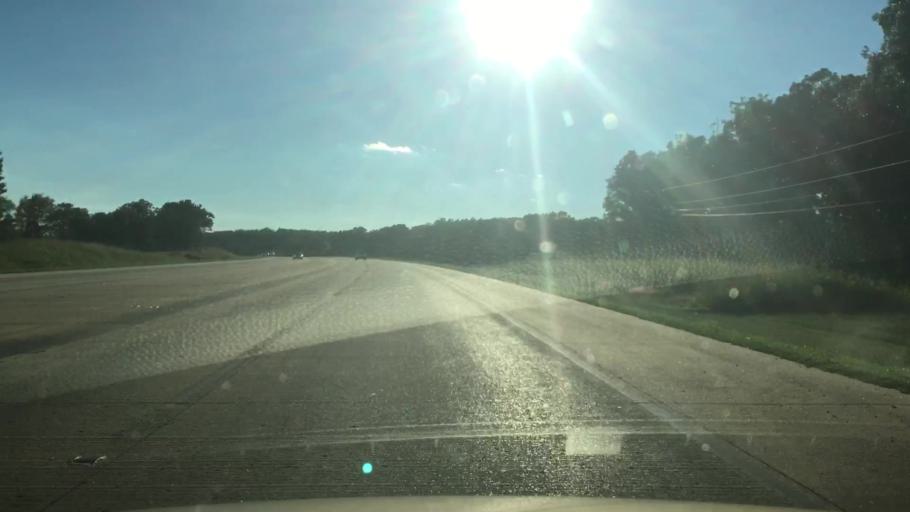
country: US
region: Oklahoma
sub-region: Cherokee County
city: Park Hill
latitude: 35.8475
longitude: -95.0245
